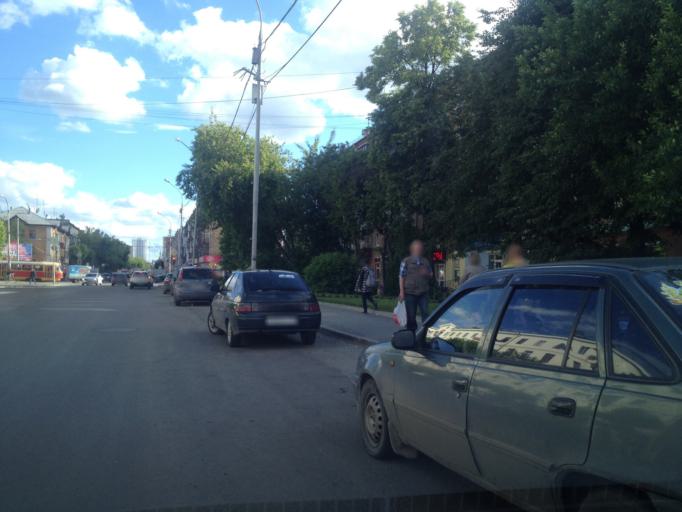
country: RU
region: Sverdlovsk
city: Yekaterinburg
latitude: 56.8370
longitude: 60.5532
